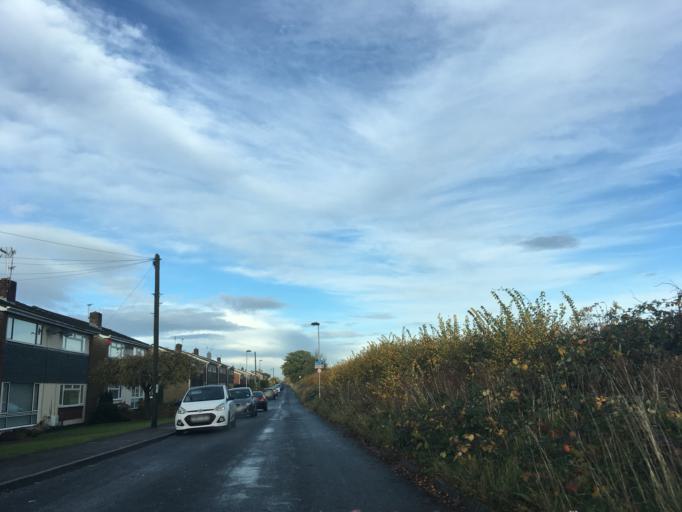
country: GB
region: England
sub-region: South Gloucestershire
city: Winterbourne
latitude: 51.5233
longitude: -2.4685
